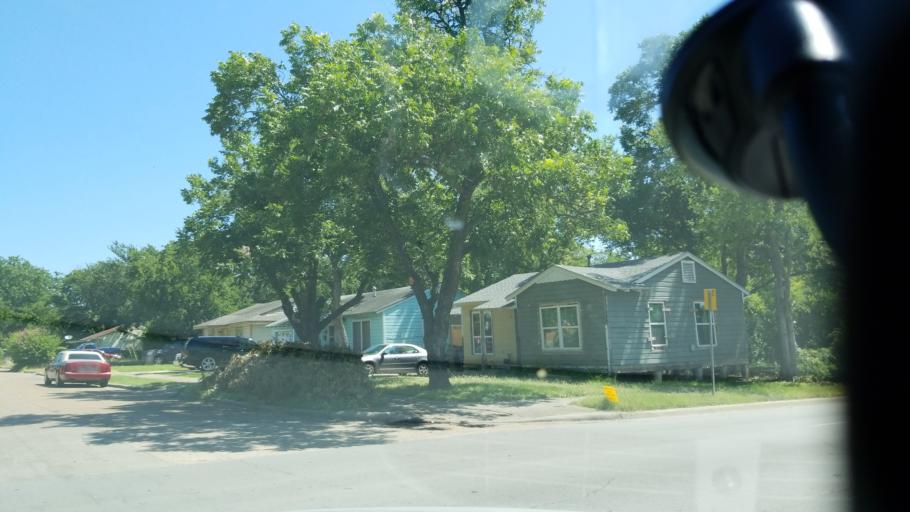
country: US
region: Texas
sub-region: Dallas County
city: Cockrell Hill
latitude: 32.7060
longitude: -96.8194
